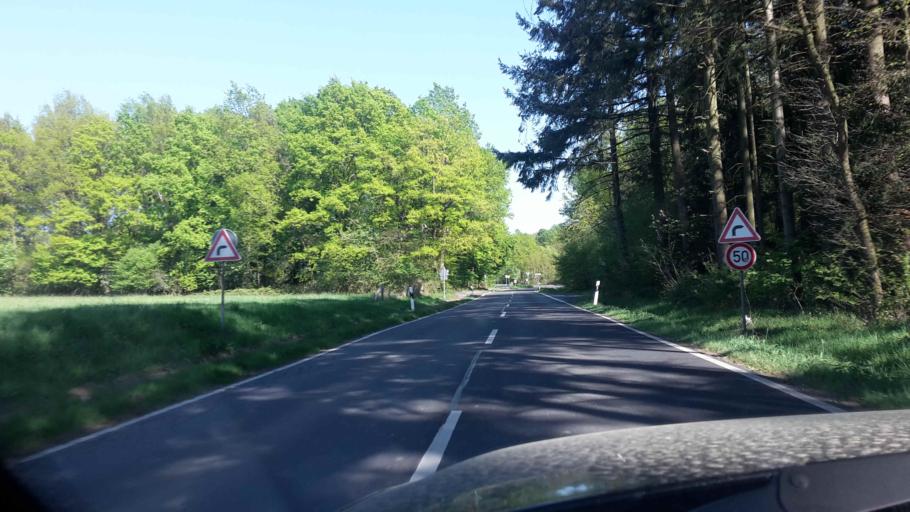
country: DE
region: North Rhine-Westphalia
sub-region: Regierungsbezirk Koln
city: Hennef
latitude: 50.7068
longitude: 7.3141
